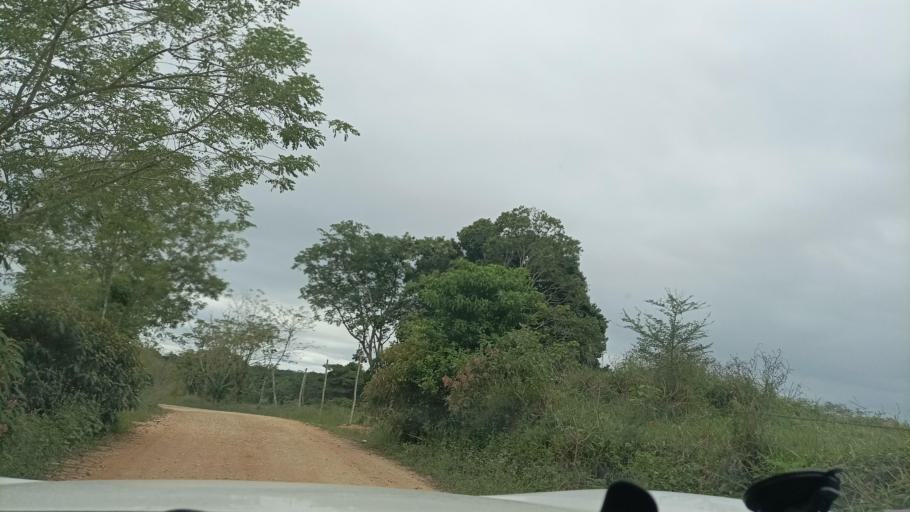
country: MX
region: Veracruz
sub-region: Uxpanapa
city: Poblado Cinco
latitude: 17.4807
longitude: -94.5709
